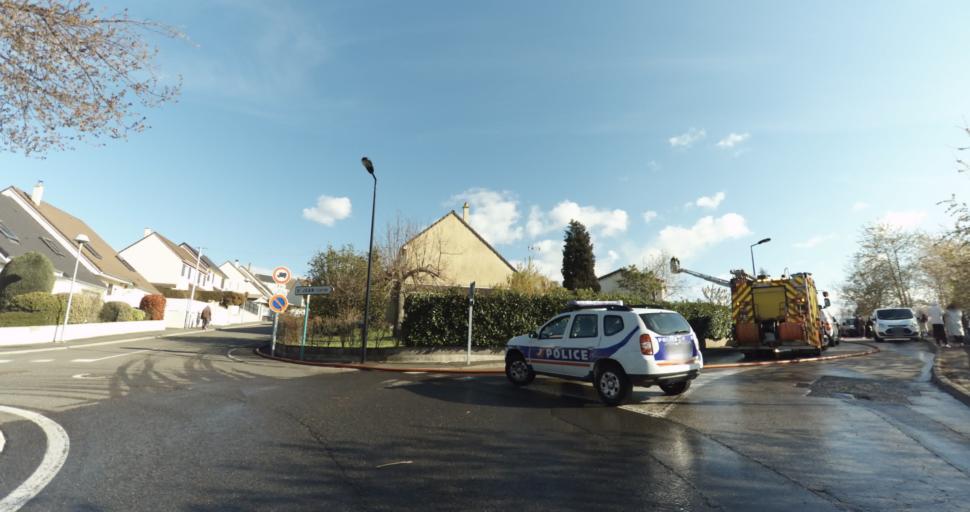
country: FR
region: Rhone-Alpes
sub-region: Departement de la Loire
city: Saint-Jean-Bonnefonds
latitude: 45.4530
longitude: 4.4278
